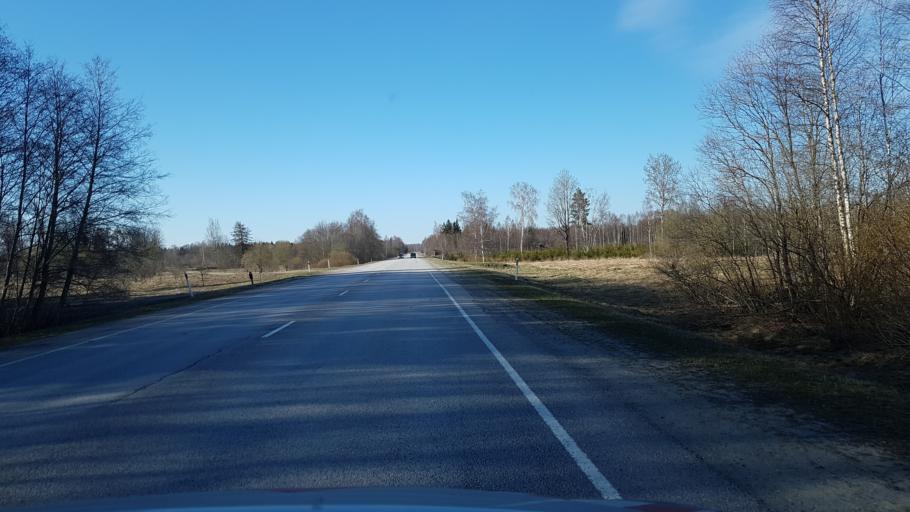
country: EE
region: Ida-Virumaa
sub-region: Johvi vald
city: Johvi
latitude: 59.1711
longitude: 27.3511
